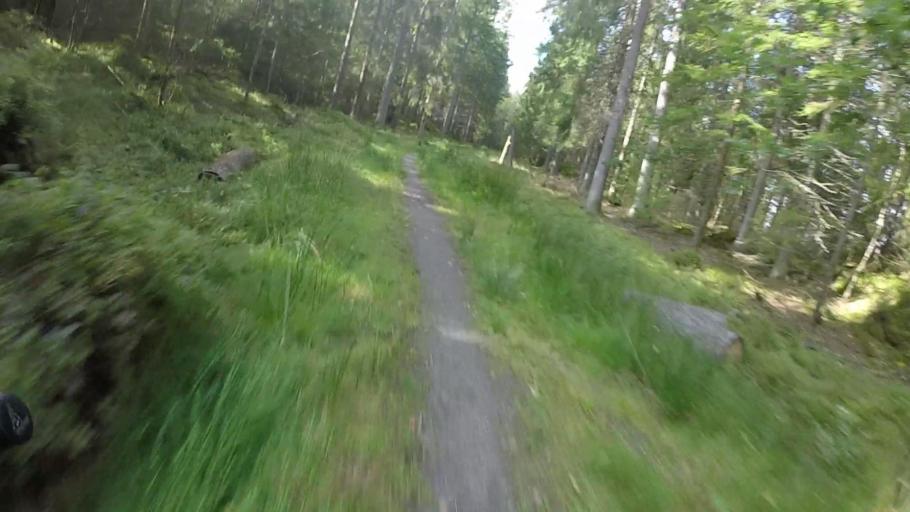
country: SE
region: Vaestra Goetaland
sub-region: Trollhattan
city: Trollhattan
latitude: 58.2573
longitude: 12.2480
